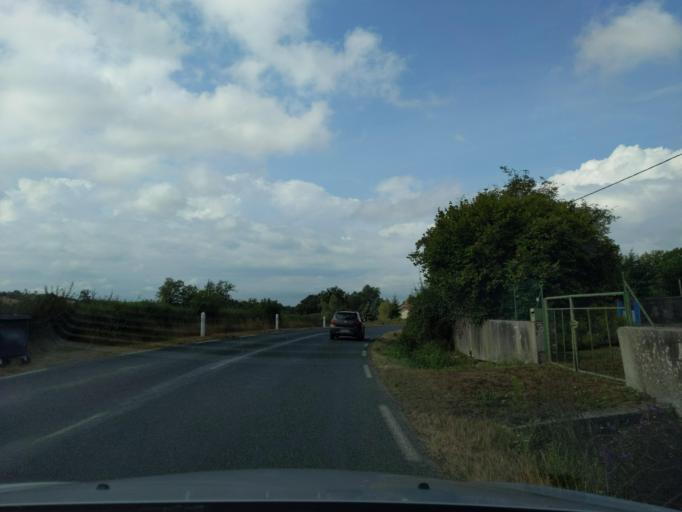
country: FR
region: Bourgogne
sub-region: Departement de Saone-et-Loire
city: Bourbon-Lancy
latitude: 46.6772
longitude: 3.8126
